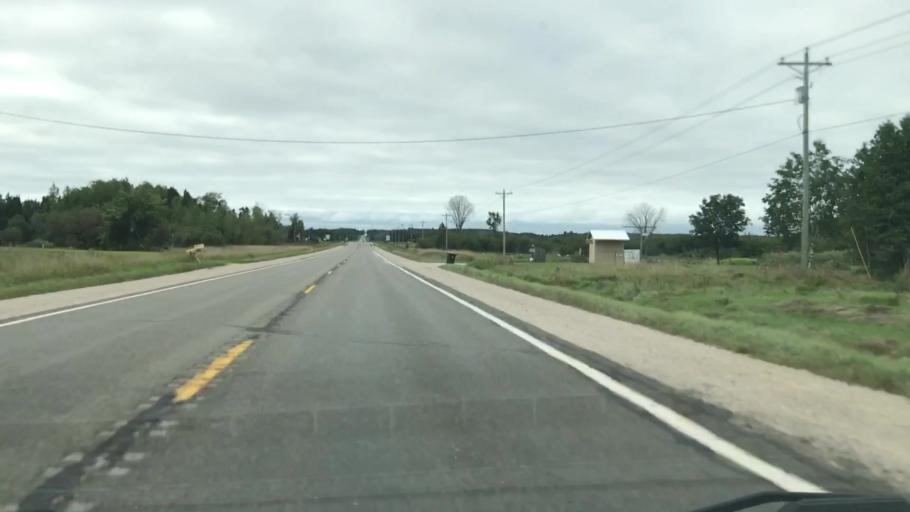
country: US
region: Michigan
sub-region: Luce County
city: Newberry
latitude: 46.1508
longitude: -85.5714
